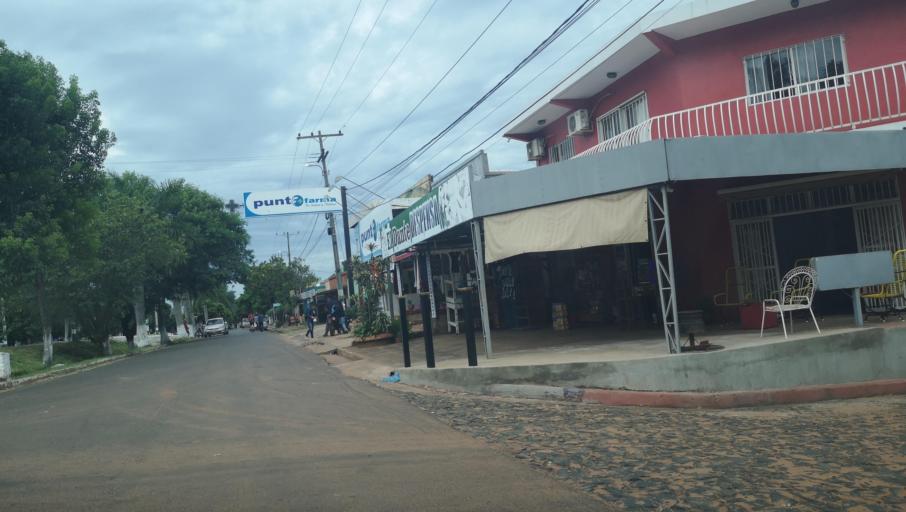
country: PY
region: San Pedro
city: Capiibary
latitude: -24.7255
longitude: -56.0180
